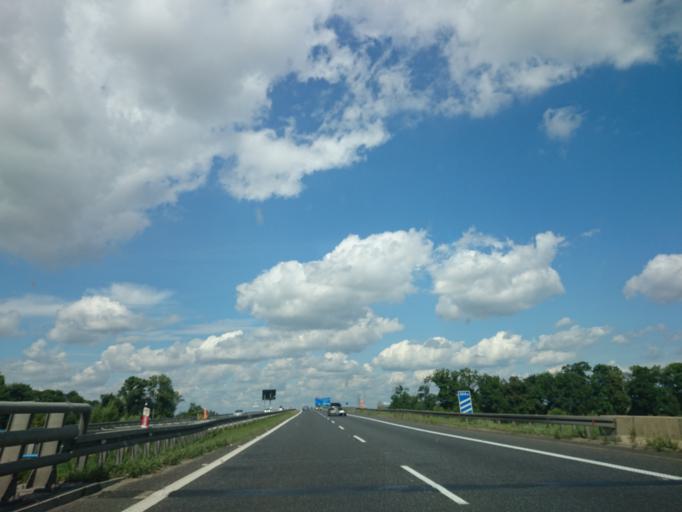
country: PL
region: Lower Silesian Voivodeship
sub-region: Powiat wroclawski
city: Bielany Wroclawskie
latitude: 51.0434
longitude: 16.9862
